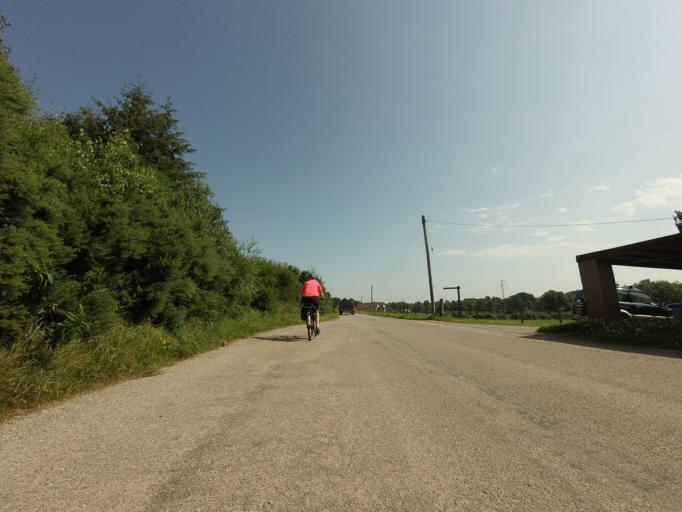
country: GB
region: Scotland
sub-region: Highland
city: Tain
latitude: 57.7607
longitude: -4.1176
